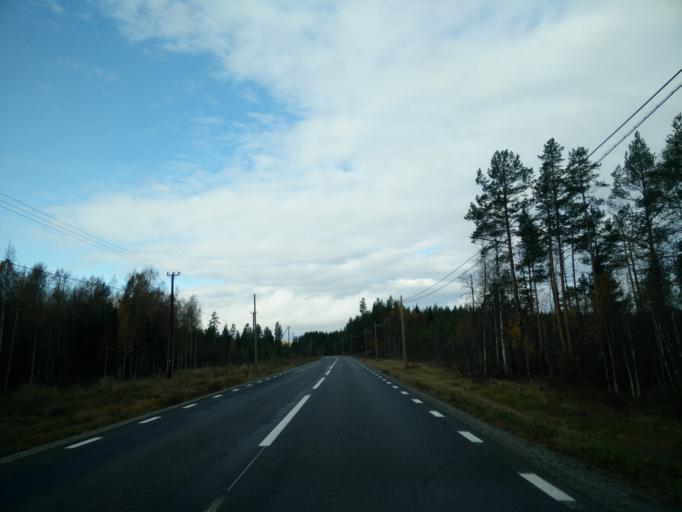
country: SE
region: Jaemtland
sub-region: Braecke Kommun
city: Braecke
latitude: 62.3970
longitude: 15.1716
